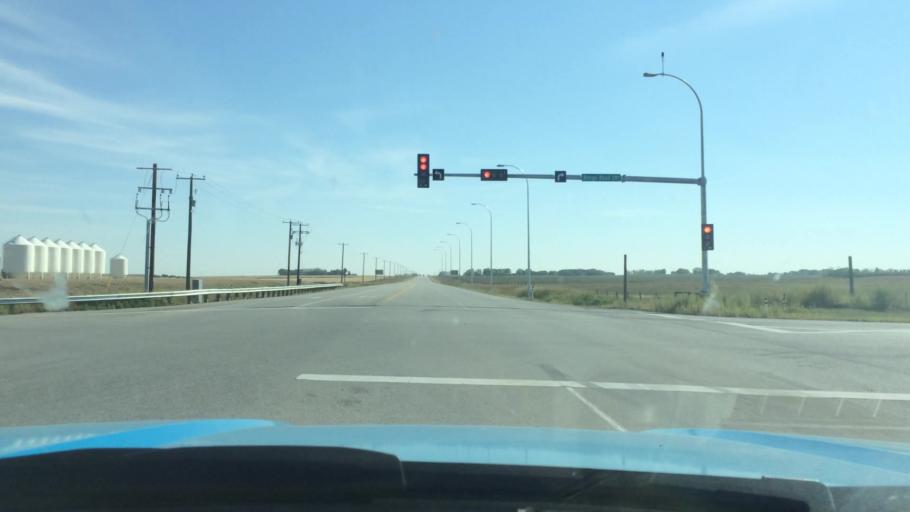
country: CA
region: Alberta
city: Airdrie
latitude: 51.2126
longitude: -113.9355
